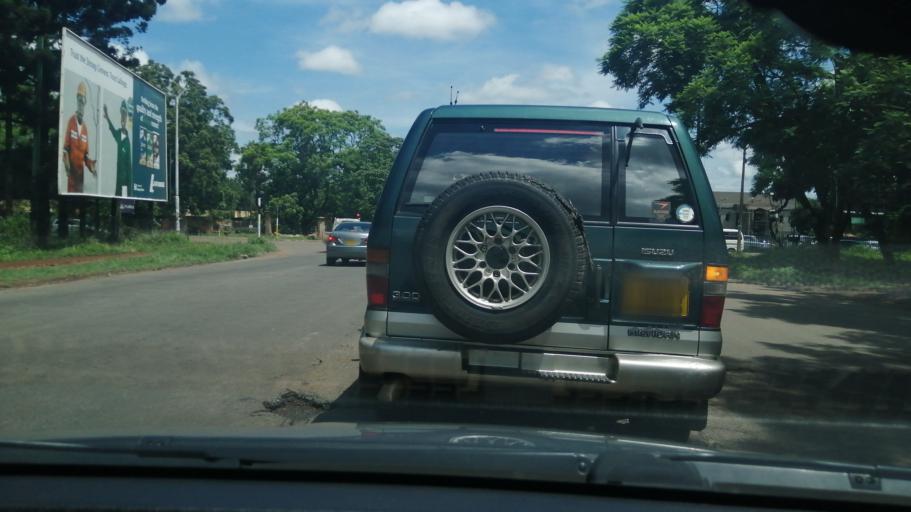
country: ZW
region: Harare
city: Harare
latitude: -17.8204
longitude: 31.0312
